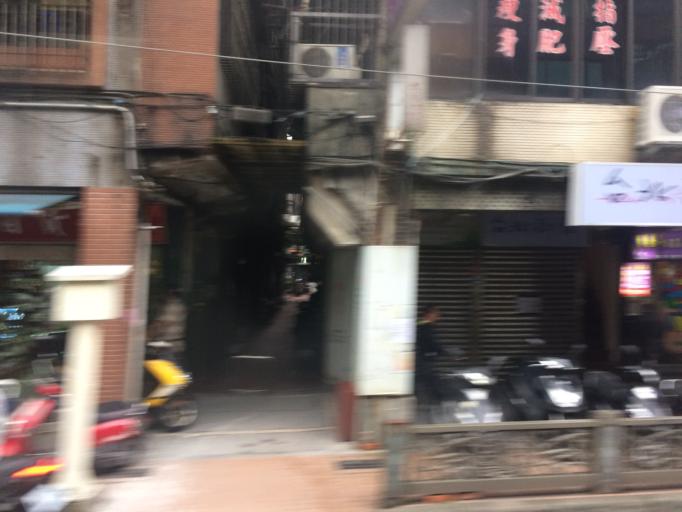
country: TW
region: Taiwan
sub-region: Keelung
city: Keelung
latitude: 25.1299
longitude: 121.7405
